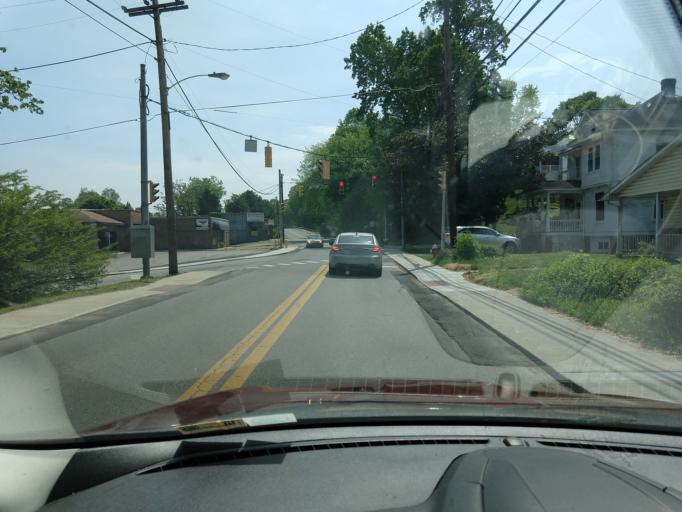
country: US
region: West Virginia
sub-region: Kanawha County
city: Saint Albans
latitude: 38.3815
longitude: -81.8260
